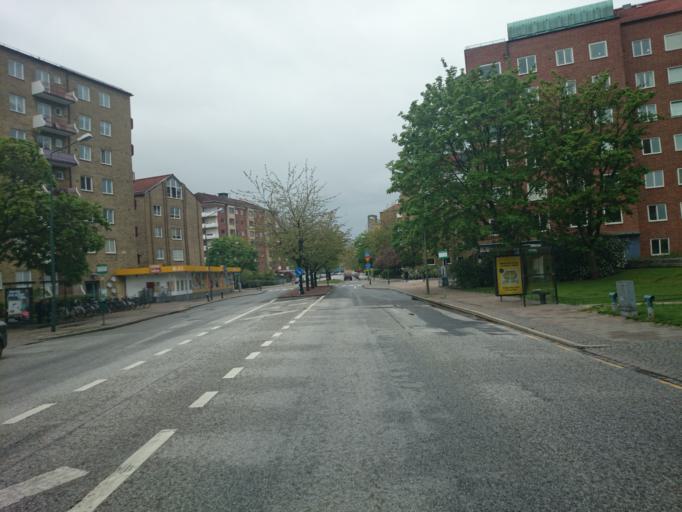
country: SE
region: Skane
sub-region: Malmo
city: Malmoe
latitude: 55.6010
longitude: 12.9762
